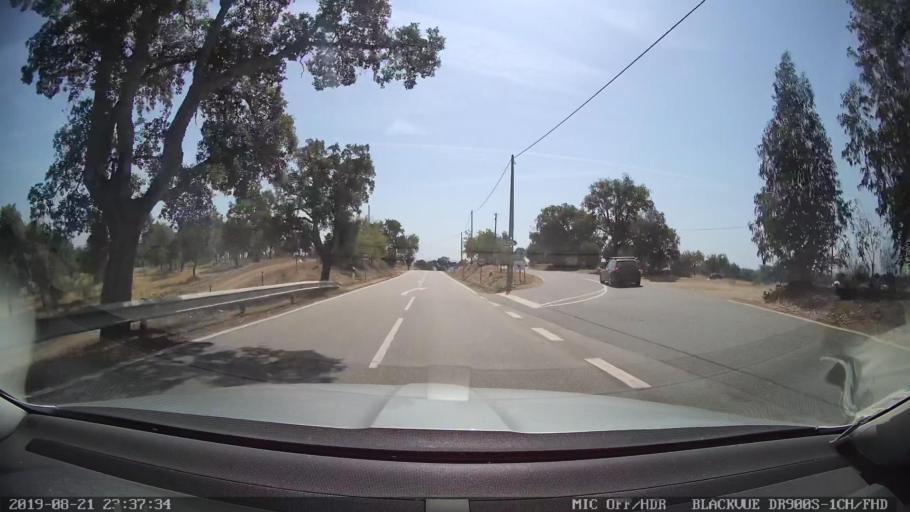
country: PT
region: Guarda
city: Alcains
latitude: 39.8674
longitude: -7.3589
